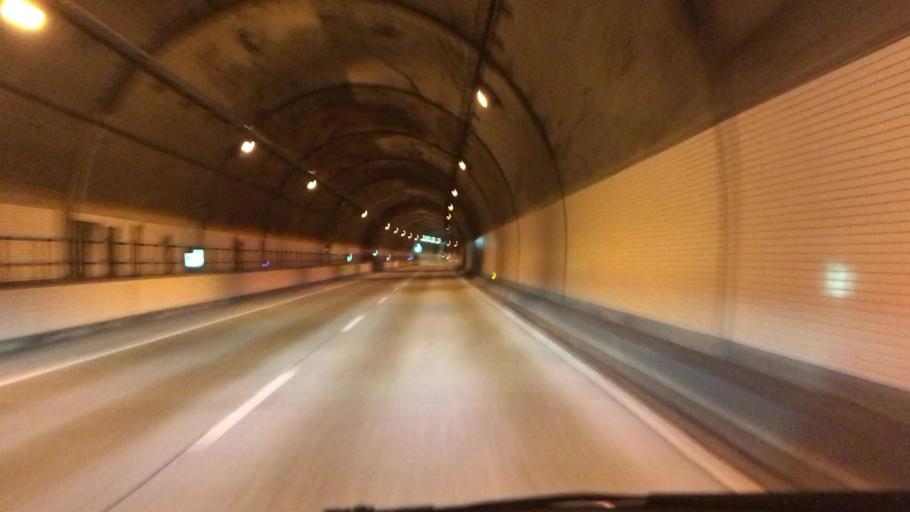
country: JP
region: Hyogo
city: Kobe
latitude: 34.7798
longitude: 135.2159
